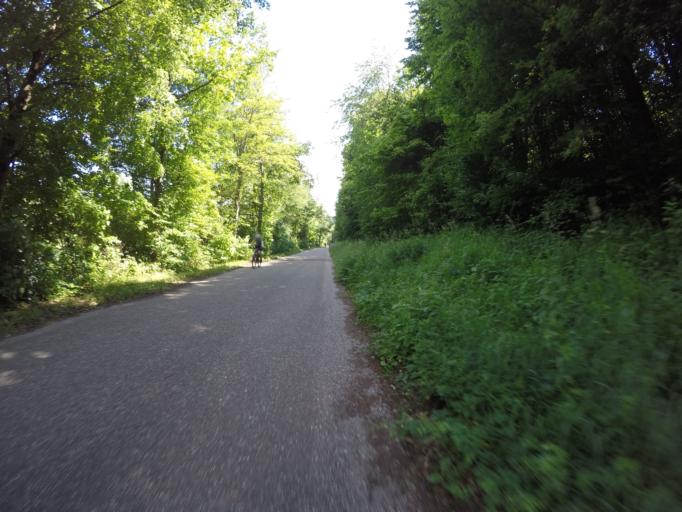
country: DE
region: Bavaria
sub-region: Lower Bavaria
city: Essing
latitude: 48.9328
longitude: 11.7880
